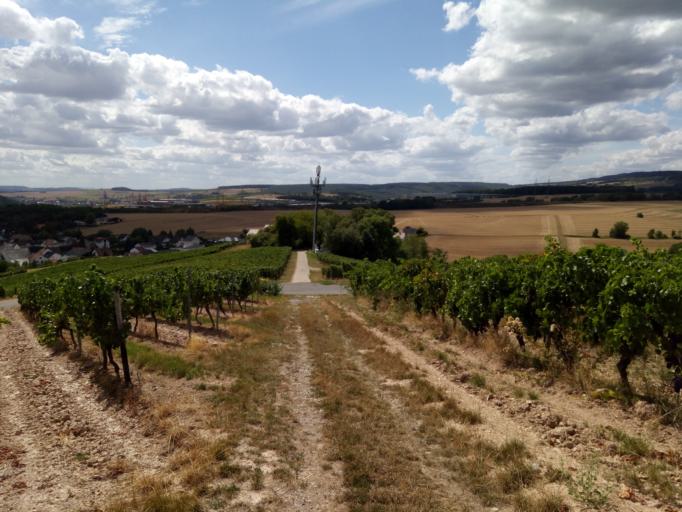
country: DE
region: Rheinland-Pfalz
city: Waldlaubersheim
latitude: 49.9336
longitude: 7.8331
